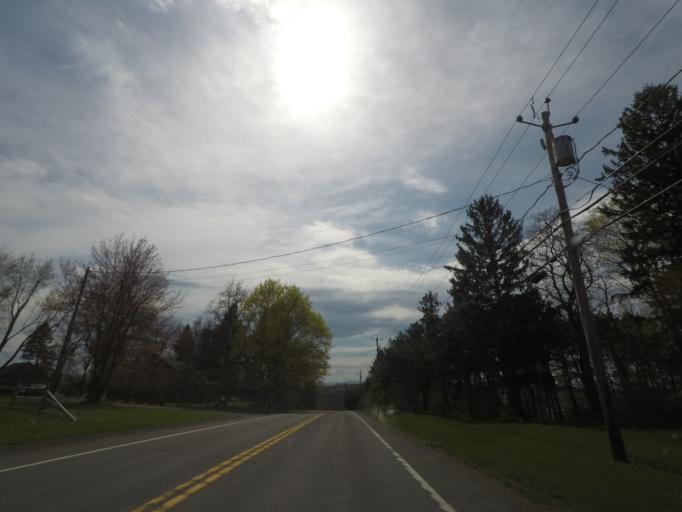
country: US
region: New York
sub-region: Columbia County
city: Philmont
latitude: 42.3052
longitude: -73.6509
